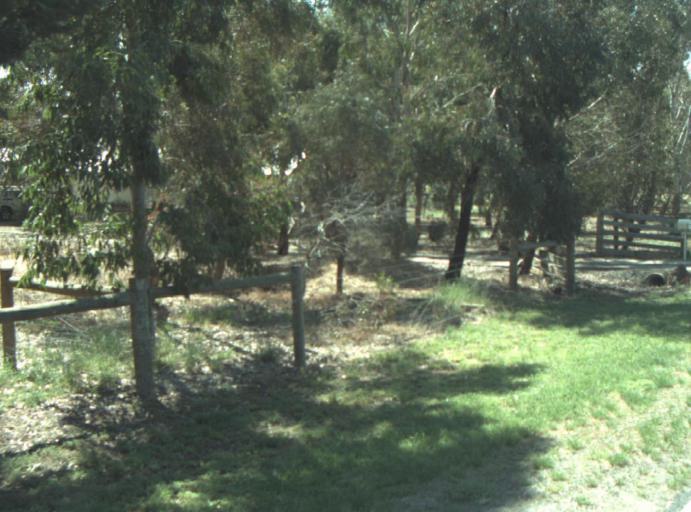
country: AU
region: Victoria
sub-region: Greater Geelong
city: Lara
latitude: -38.0016
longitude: 144.4001
